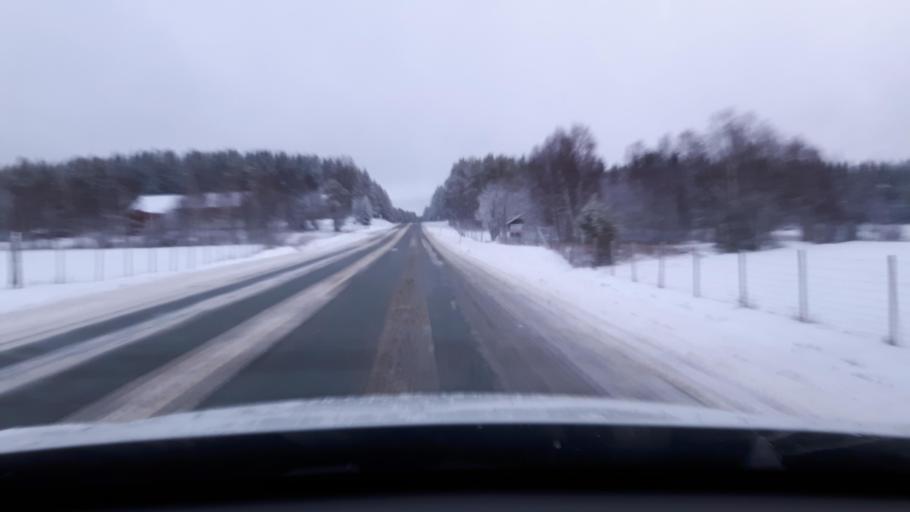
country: SE
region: Vaesterbotten
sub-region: Robertsfors Kommun
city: Robertsfors
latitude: 64.0026
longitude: 20.7965
